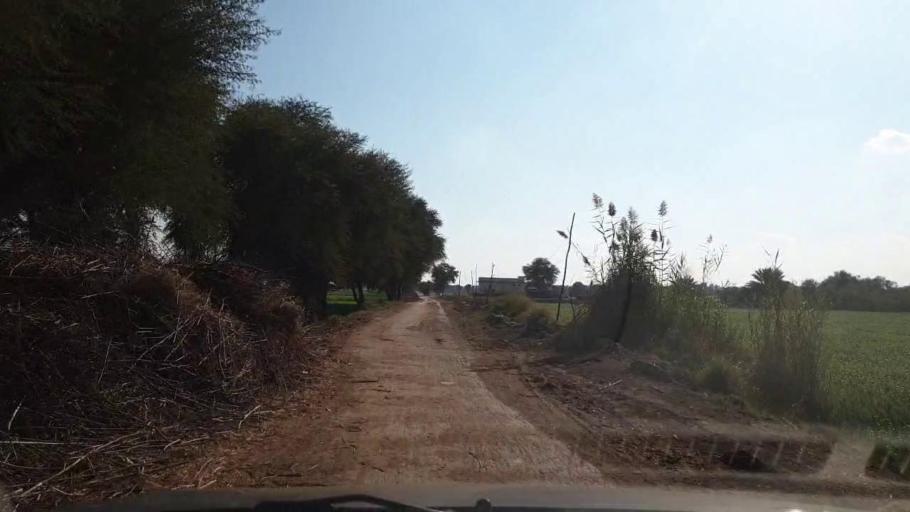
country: PK
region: Sindh
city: Sinjhoro
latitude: 25.9867
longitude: 68.7264
